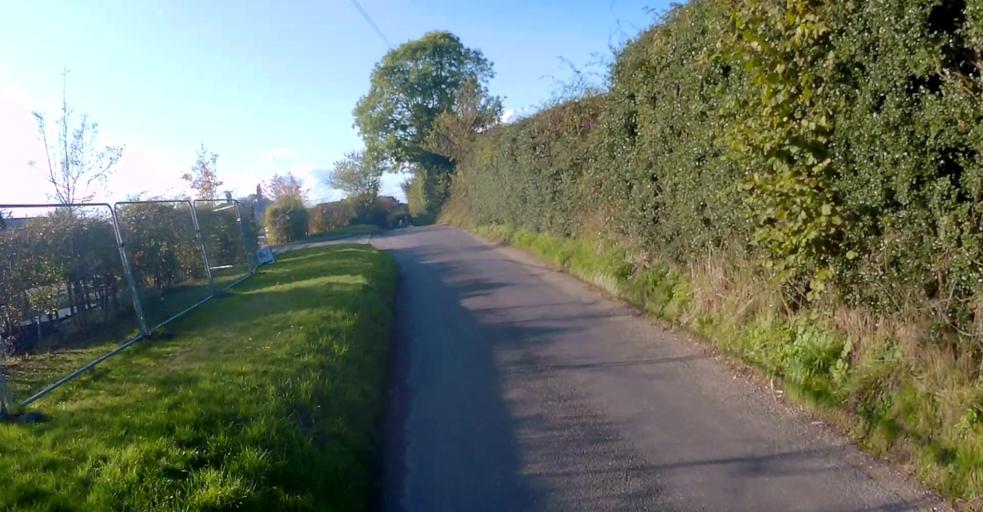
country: GB
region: England
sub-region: Hampshire
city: Long Sutton
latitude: 51.2123
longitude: -0.9092
